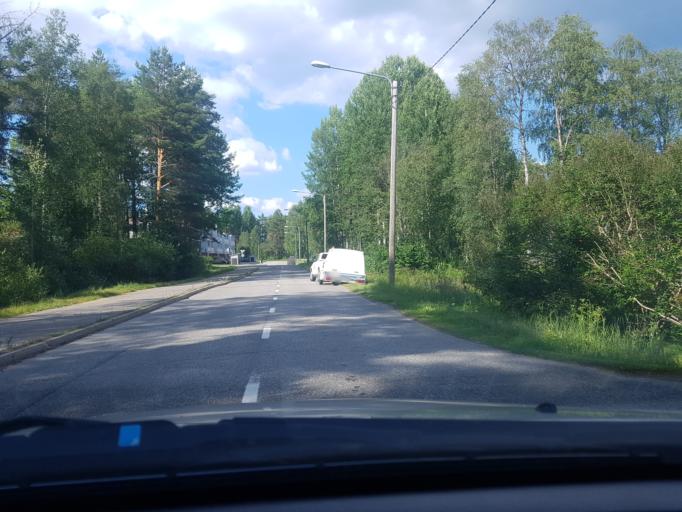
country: FI
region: Kainuu
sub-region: Kehys-Kainuu
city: Kuhmo
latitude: 64.1320
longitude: 29.5443
